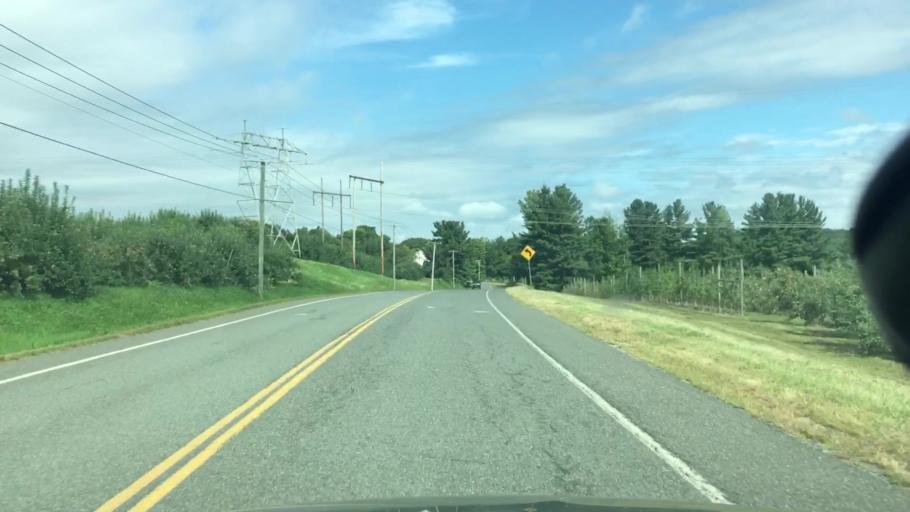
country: US
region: Massachusetts
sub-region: Franklin County
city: Colrain
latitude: 42.6525
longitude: -72.6767
